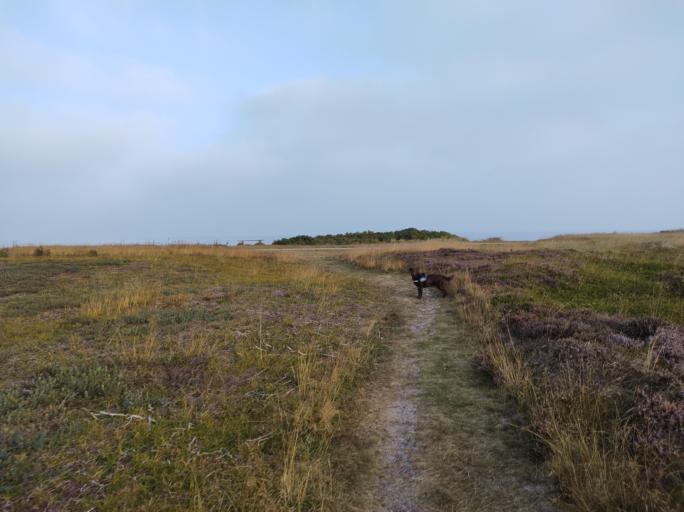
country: DK
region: Central Jutland
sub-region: Ringkobing-Skjern Kommune
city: Skjern
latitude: 55.8832
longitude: 8.3460
